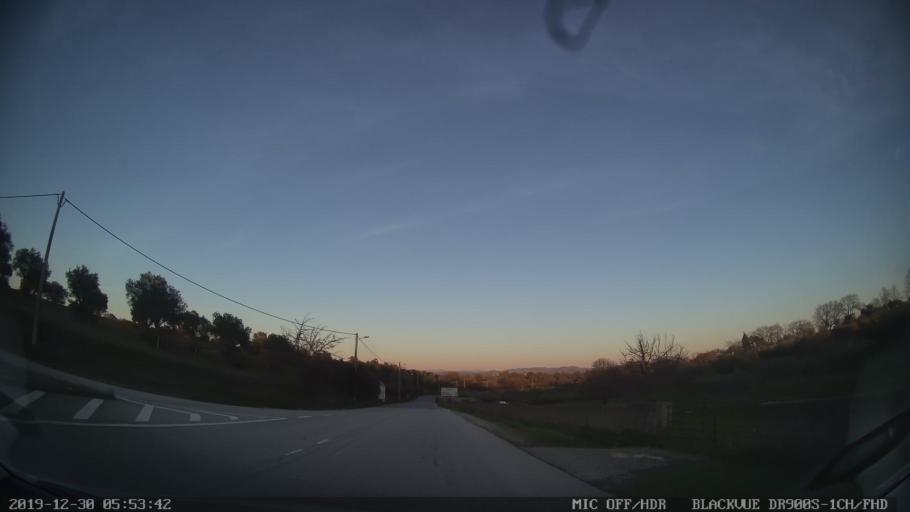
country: PT
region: Castelo Branco
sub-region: Idanha-A-Nova
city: Idanha-a-Nova
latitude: 40.0177
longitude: -7.2509
